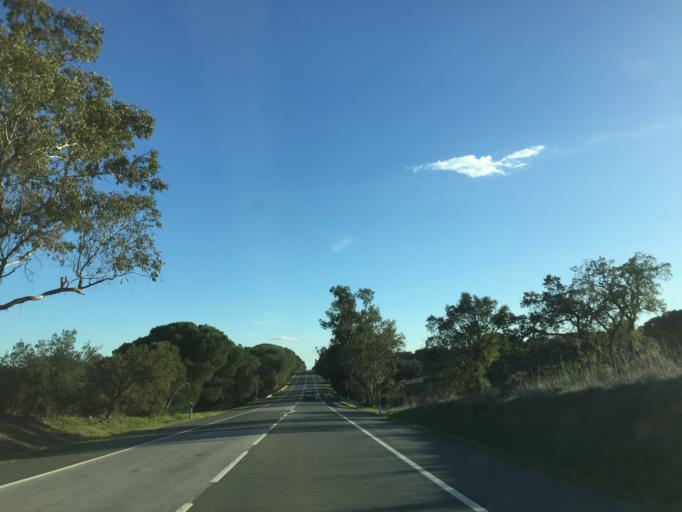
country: PT
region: Setubal
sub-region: Grandola
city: Grandola
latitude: 38.0896
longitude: -8.4180
